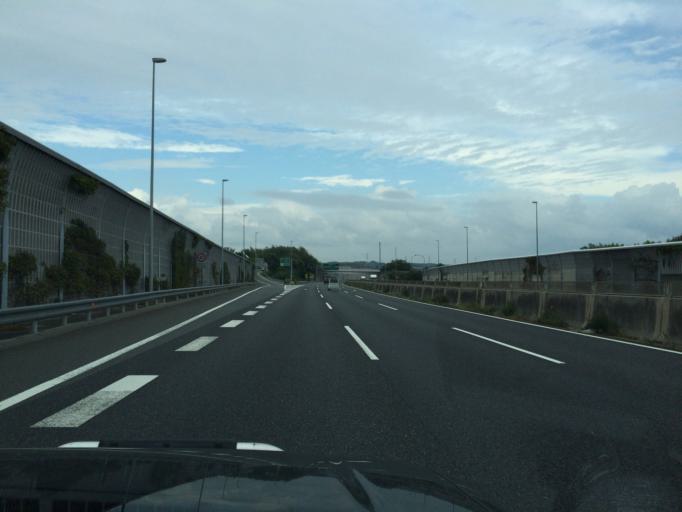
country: JP
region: Mie
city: Yokkaichi
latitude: 35.0244
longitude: 136.6024
